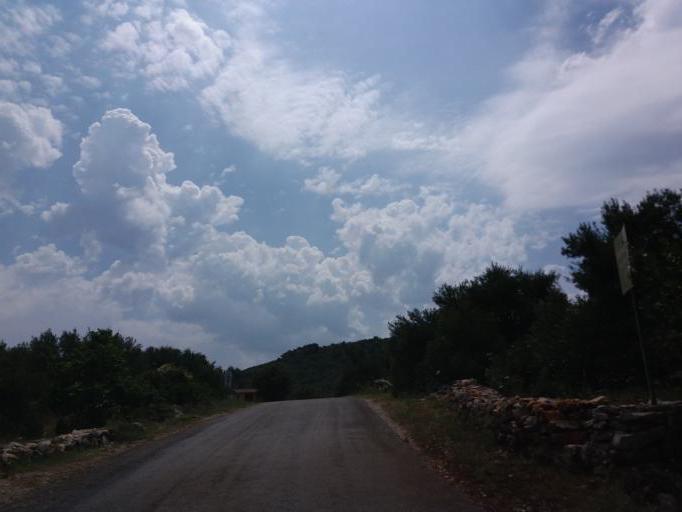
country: HR
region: Zadarska
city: Sali
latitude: 43.9352
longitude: 15.1458
